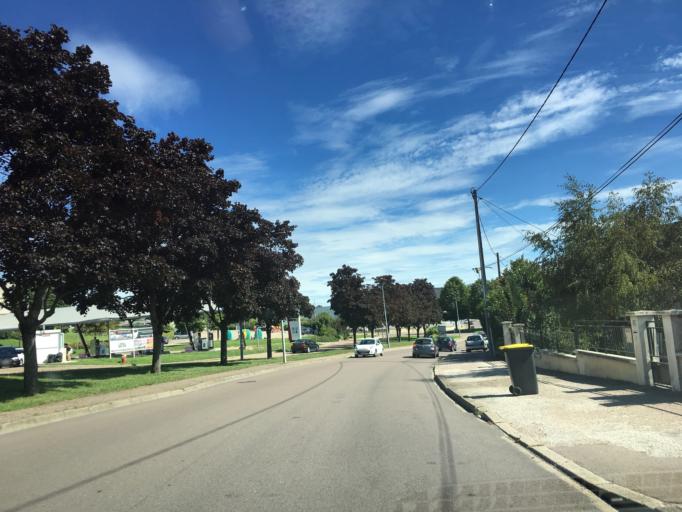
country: FR
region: Bourgogne
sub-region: Departement de l'Yonne
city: Auxerre
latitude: 47.8084
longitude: 3.5586
